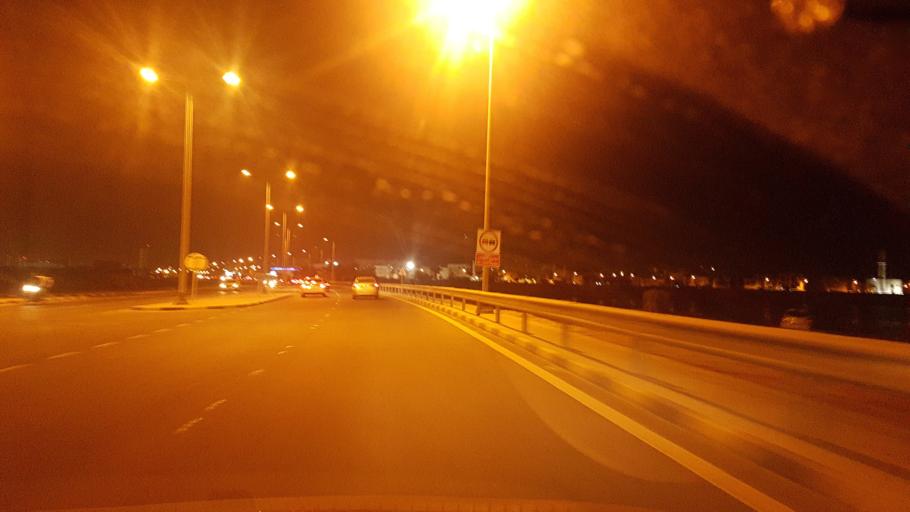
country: BH
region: Muharraq
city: Al Hadd
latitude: 26.2594
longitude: 50.6560
